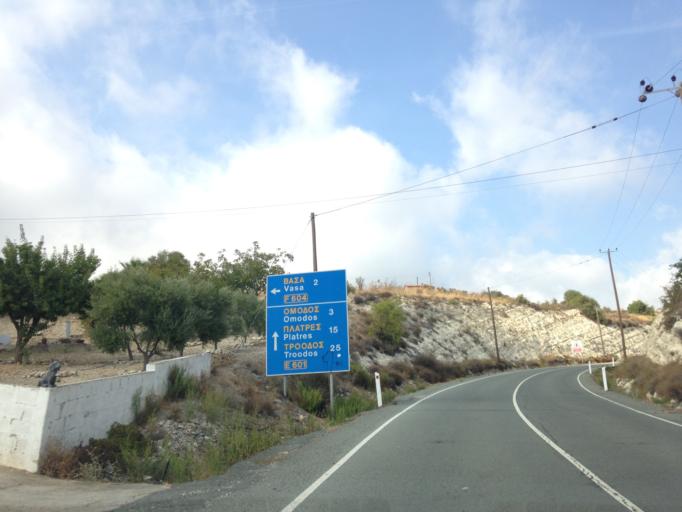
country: CY
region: Limassol
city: Pachna
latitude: 34.8253
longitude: 32.7993
